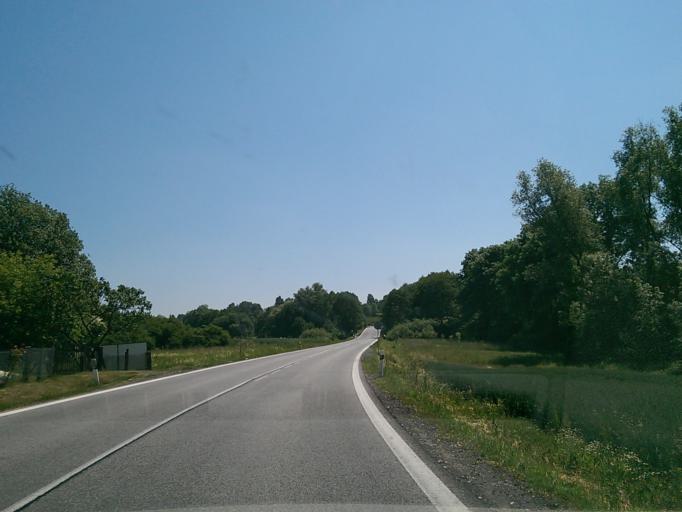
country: CZ
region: Liberecky
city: Rovensko pod Troskami
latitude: 50.4953
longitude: 15.3103
